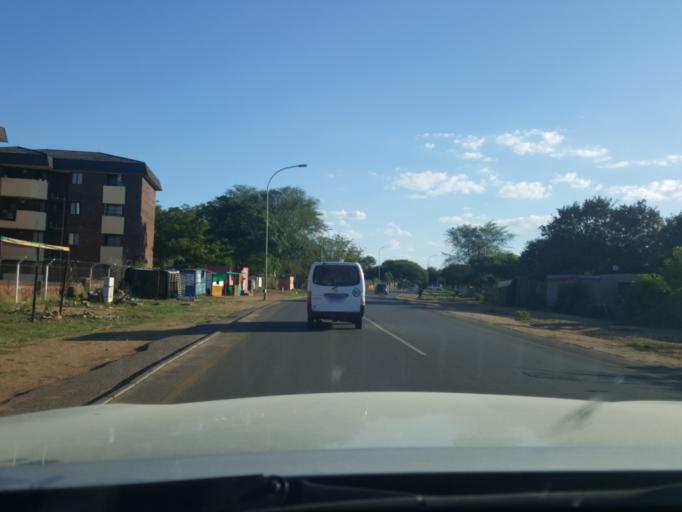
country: BW
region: South East
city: Gaborone
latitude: -24.6434
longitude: 25.9375
